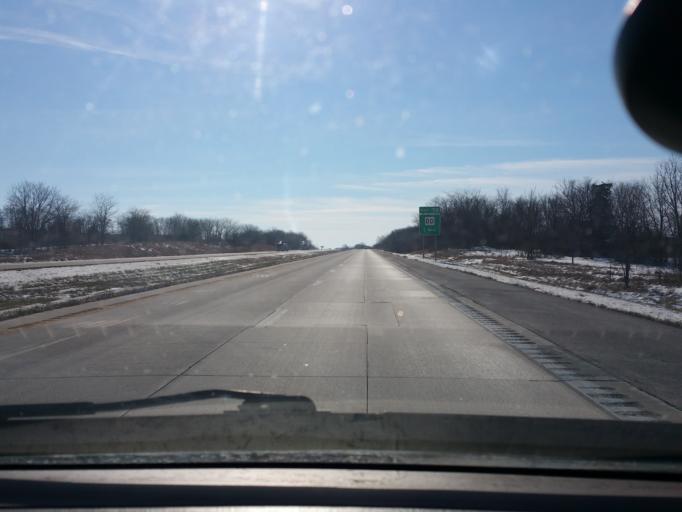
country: US
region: Missouri
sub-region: Daviess County
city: Gallatin
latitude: 40.0140
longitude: -94.0963
